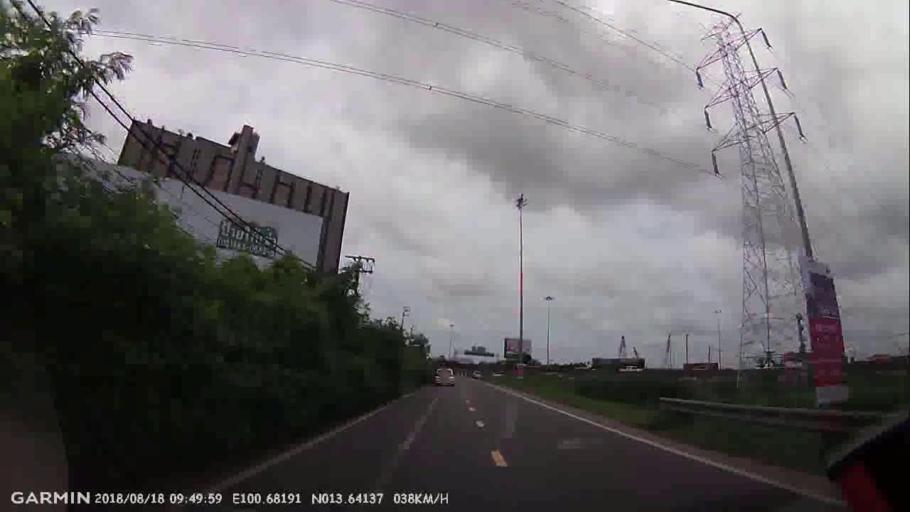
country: TH
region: Bangkok
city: Bang Na
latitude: 13.6413
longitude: 100.6818
